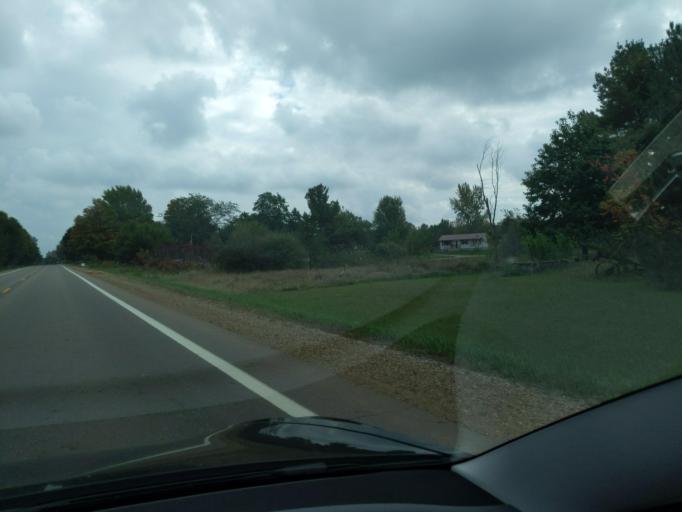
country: US
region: Michigan
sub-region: Eaton County
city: Eaton Rapids
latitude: 42.5363
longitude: -84.7268
